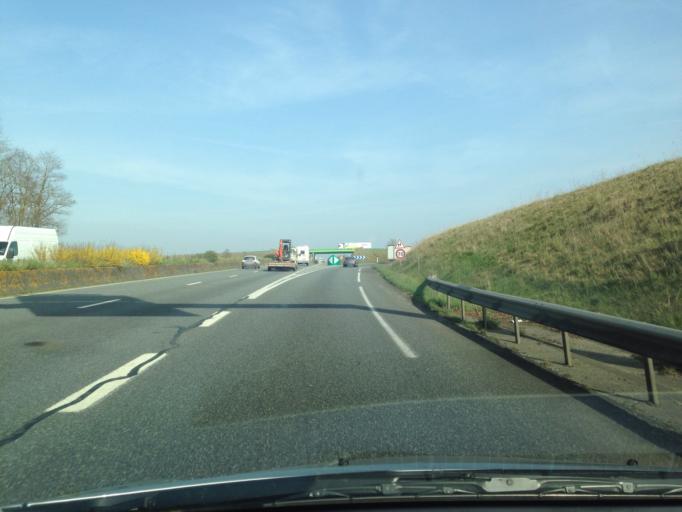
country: FR
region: Picardie
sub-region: Departement de la Somme
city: Abbeville
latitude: 50.1313
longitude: 1.8099
